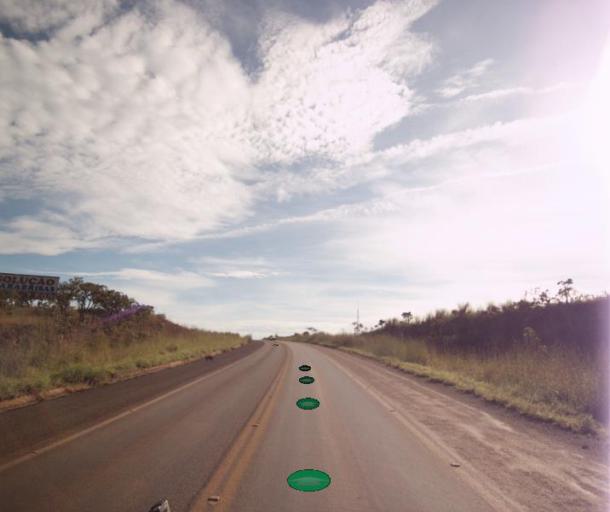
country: BR
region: Federal District
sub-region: Brasilia
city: Brasilia
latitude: -15.7507
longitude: -48.4124
